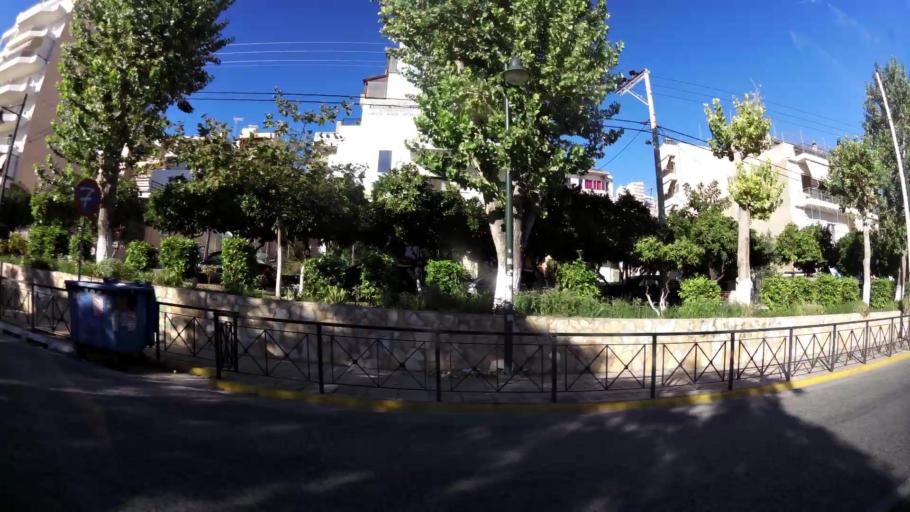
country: GR
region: Attica
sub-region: Nomos Piraios
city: Perama
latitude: 37.9634
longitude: 23.5747
